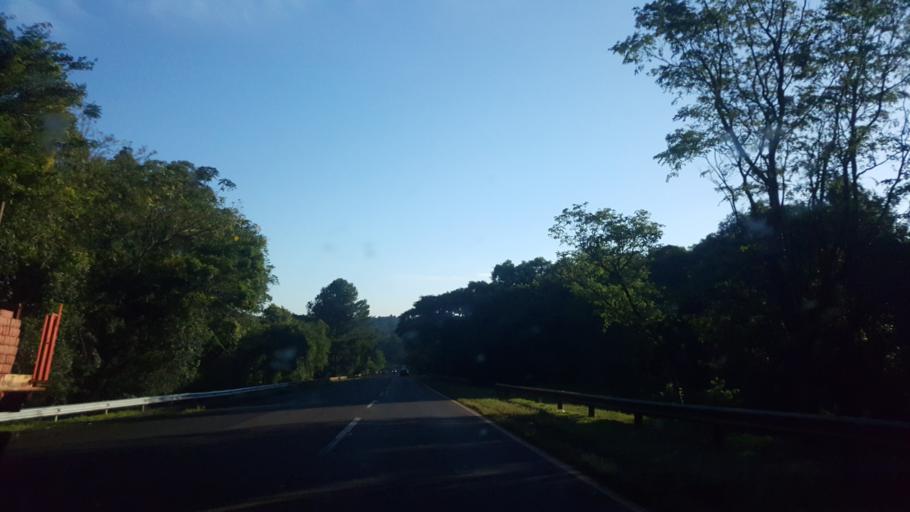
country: AR
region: Misiones
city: El Alcazar
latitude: -26.7296
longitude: -54.8709
